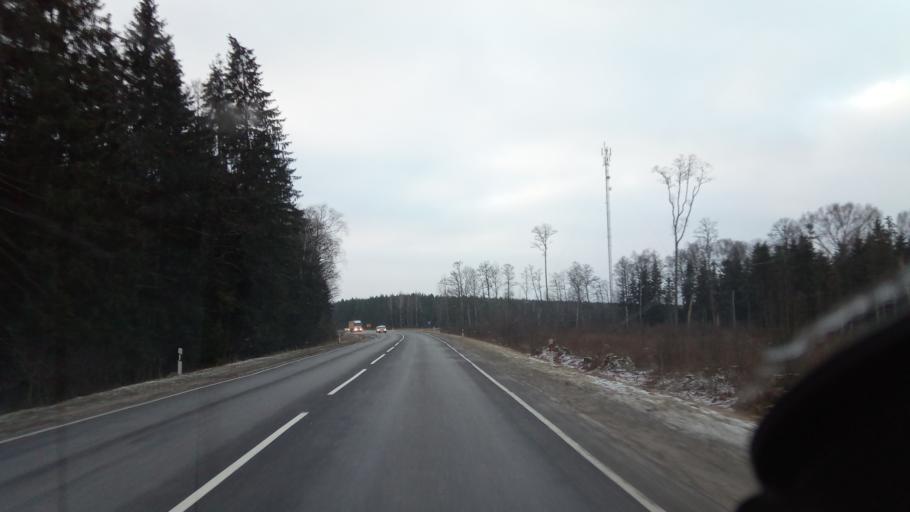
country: LT
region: Vilnius County
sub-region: Trakai
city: Rudiskes
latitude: 54.4293
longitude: 24.9797
